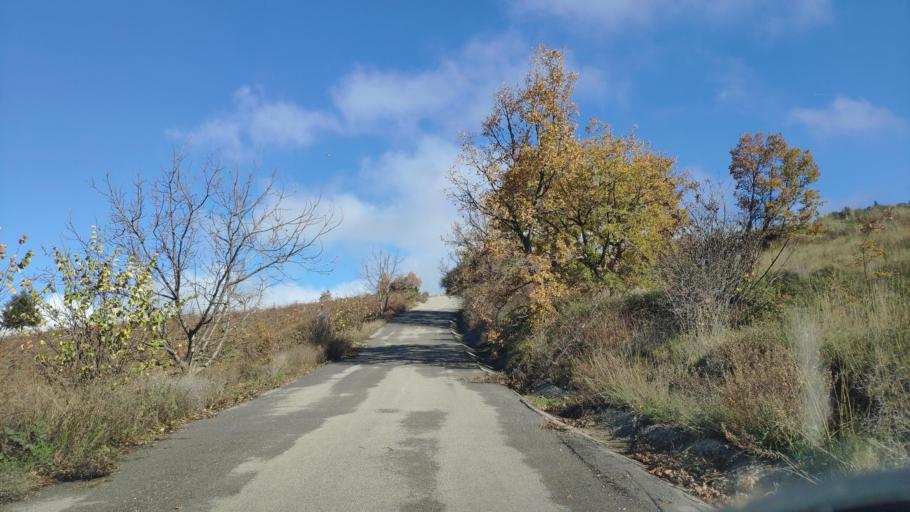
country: GR
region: West Greece
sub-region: Nomos Achaias
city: Aiyira
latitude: 38.0661
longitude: 22.4648
